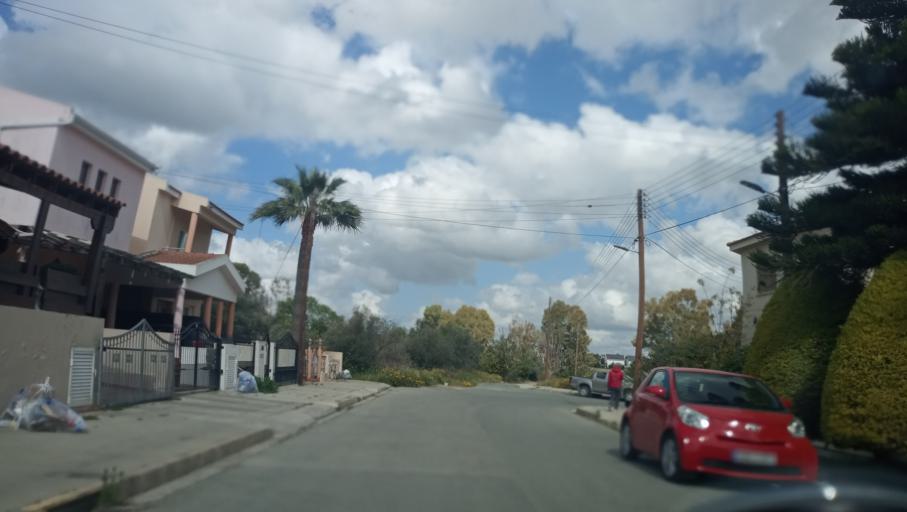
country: CY
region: Lefkosia
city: Tseri
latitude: 35.1185
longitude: 33.3100
